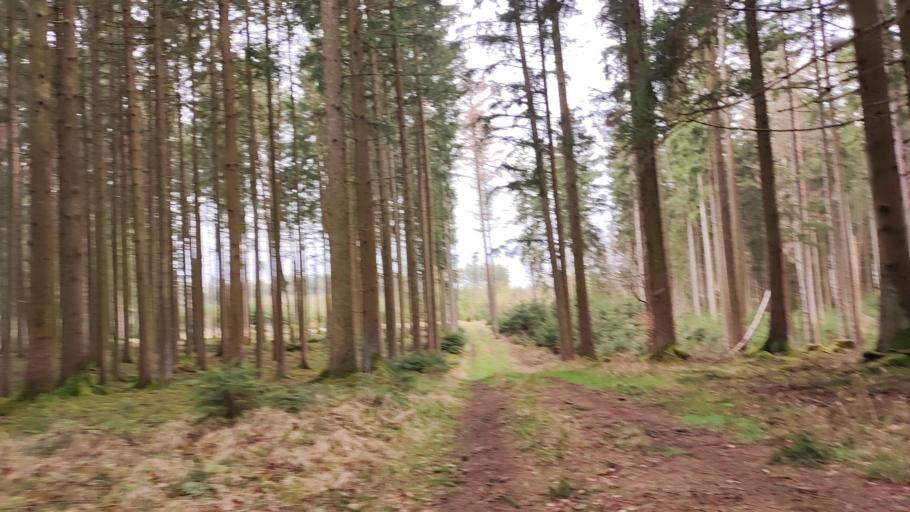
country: DE
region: Bavaria
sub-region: Swabia
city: Altenmunster
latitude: 48.4333
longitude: 10.5660
